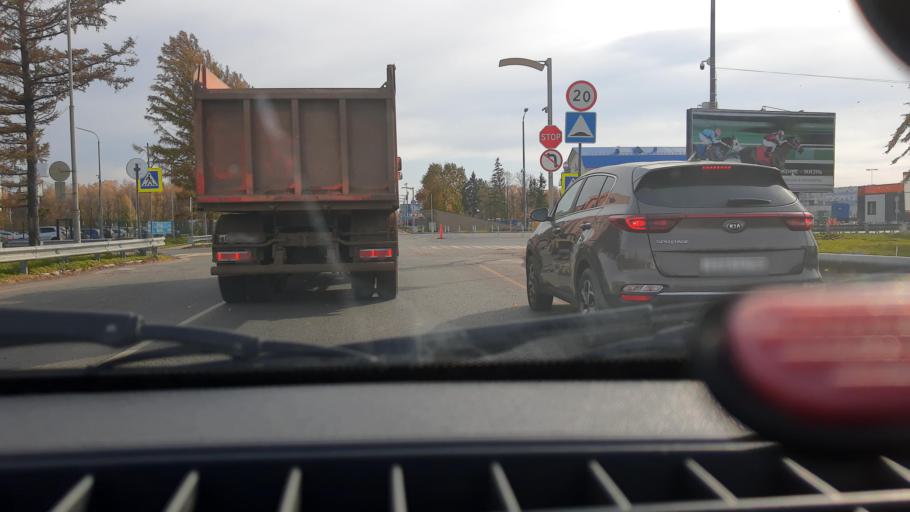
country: RU
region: Bashkortostan
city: Ufa
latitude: 54.5687
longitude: 55.8860
